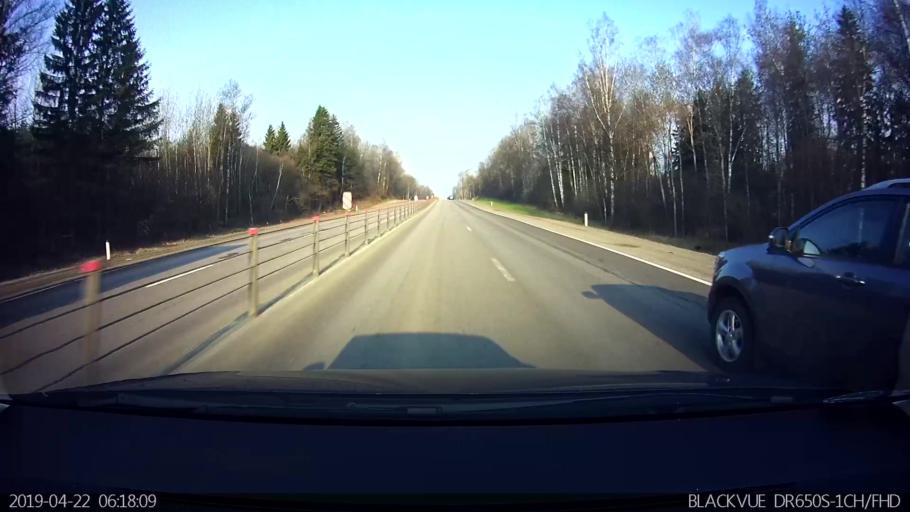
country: RU
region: Moskovskaya
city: Mozhaysk
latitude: 55.4627
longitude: 35.9685
